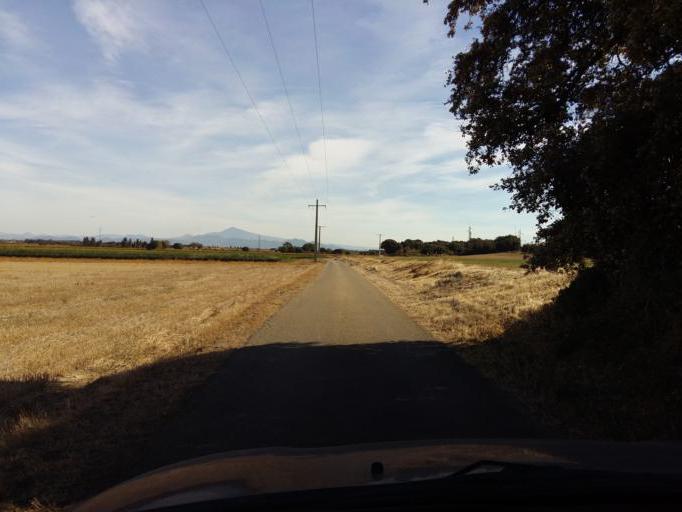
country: FR
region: Provence-Alpes-Cote d'Azur
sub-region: Departement du Vaucluse
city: Piolenc
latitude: 44.1751
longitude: 4.7821
